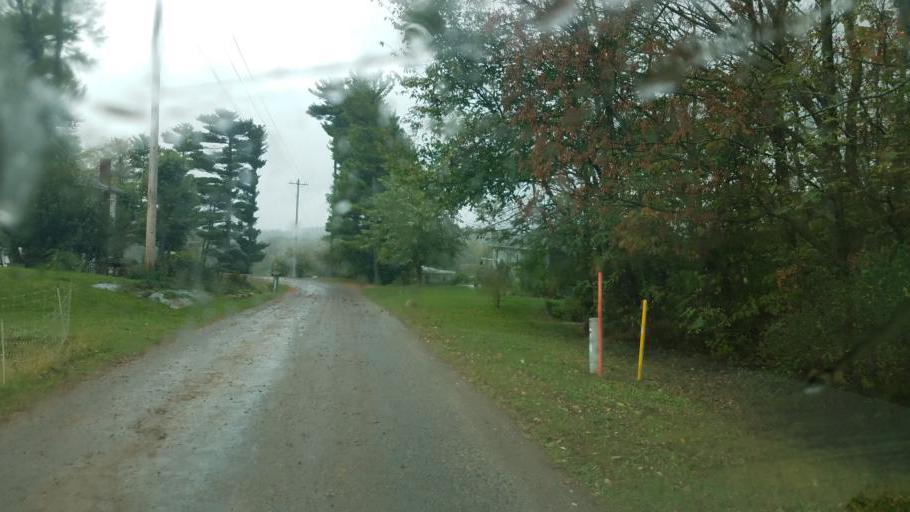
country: US
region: Ohio
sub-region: Holmes County
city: Millersburg
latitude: 40.5837
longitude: -81.8609
